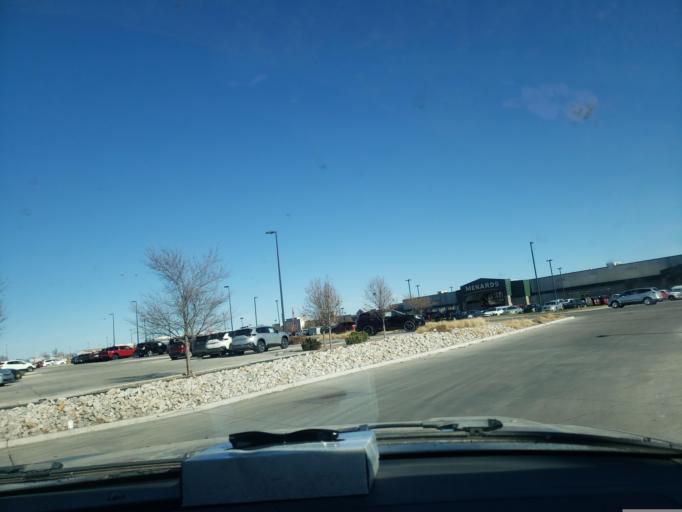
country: US
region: Kansas
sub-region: Finney County
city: Garden City
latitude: 37.9755
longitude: -100.8372
